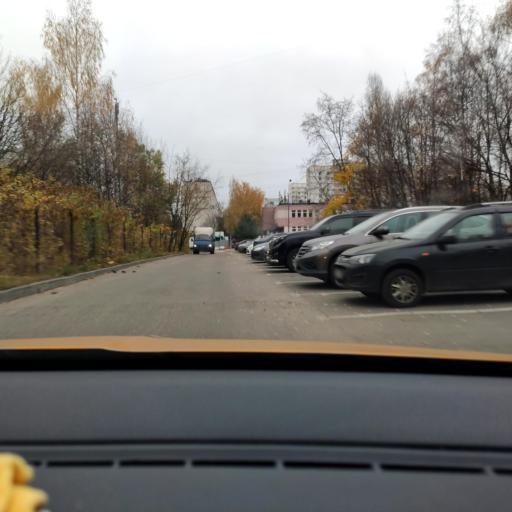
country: RU
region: Moscow
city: Tyoply Stan
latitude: 55.6272
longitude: 37.4837
